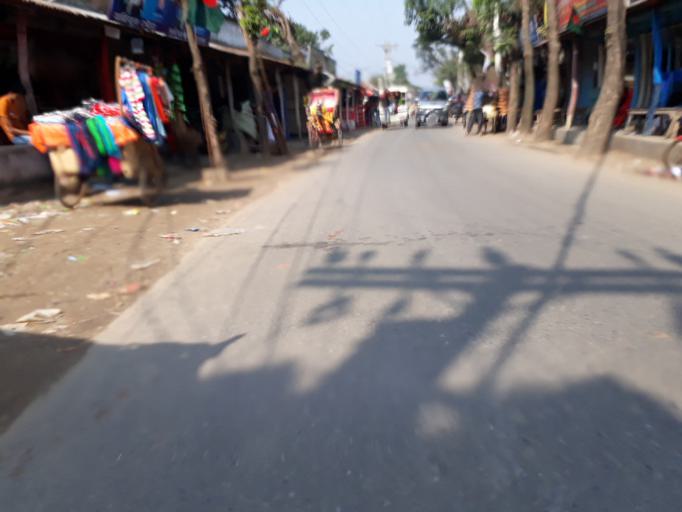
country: BD
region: Dhaka
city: Tungi
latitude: 23.8785
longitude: 90.3103
